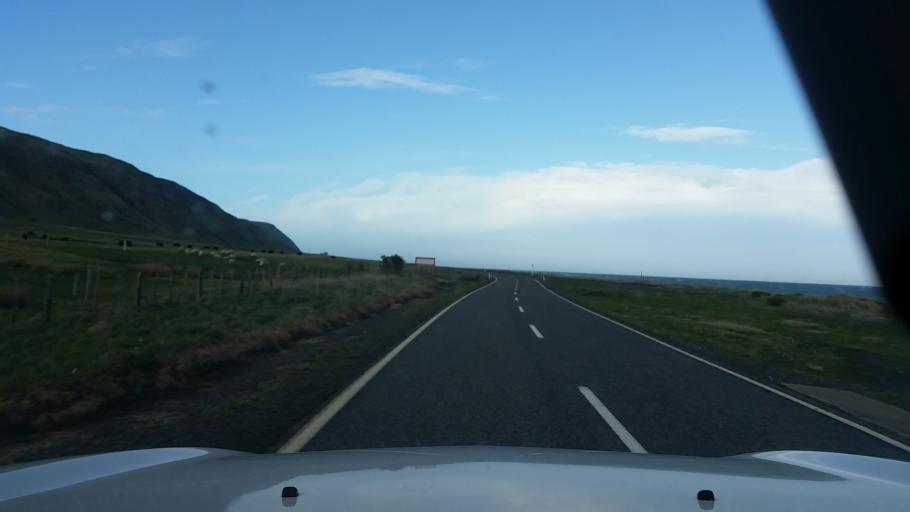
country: NZ
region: Wellington
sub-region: South Wairarapa District
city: Waipawa
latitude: -41.5616
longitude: 175.2220
